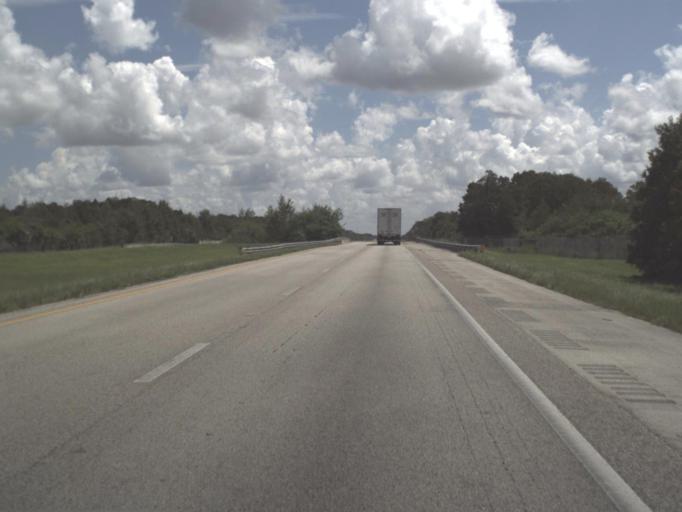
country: US
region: Florida
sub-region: Collier County
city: Orangetree
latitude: 26.1532
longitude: -81.4500
